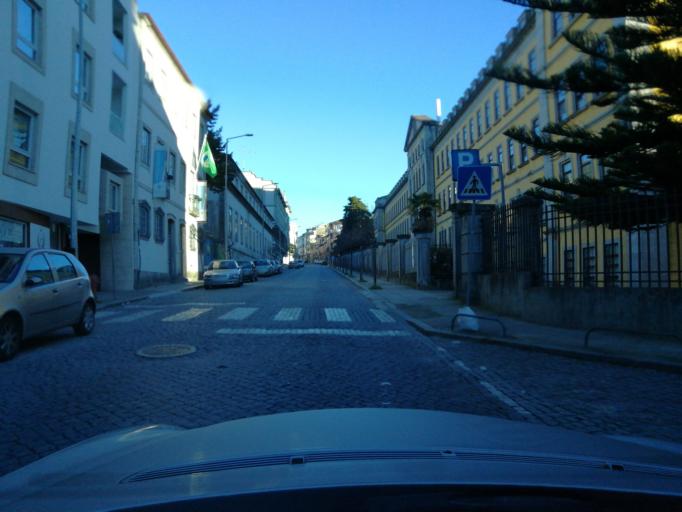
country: PT
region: Braga
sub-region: Braga
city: Braga
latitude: 41.5532
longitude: -8.4171
